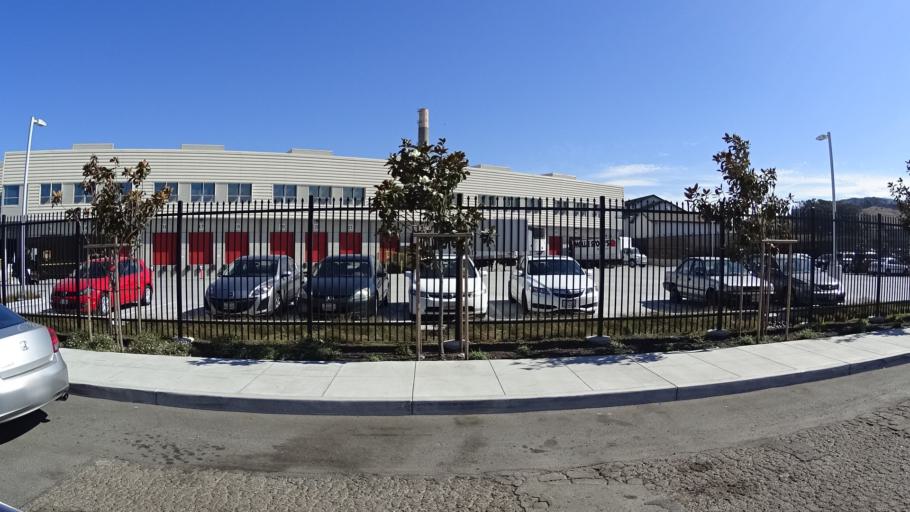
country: US
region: California
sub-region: San Francisco County
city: San Francisco
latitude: 37.7410
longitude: -122.3958
